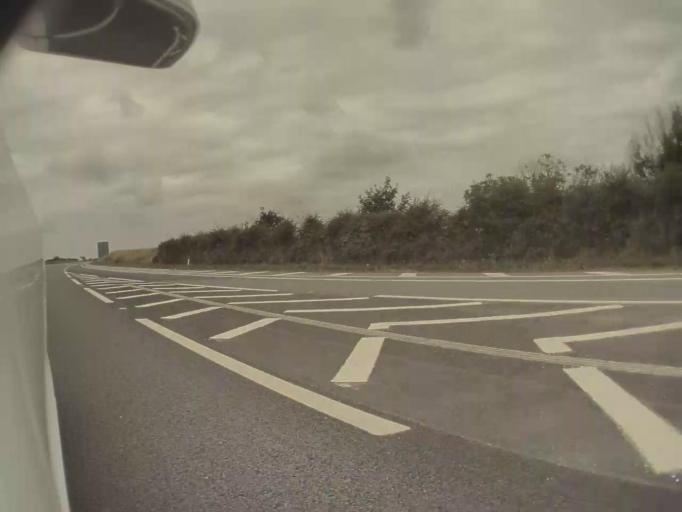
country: GB
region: Wales
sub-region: Anglesey
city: Valley
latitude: 53.2778
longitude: -4.5535
